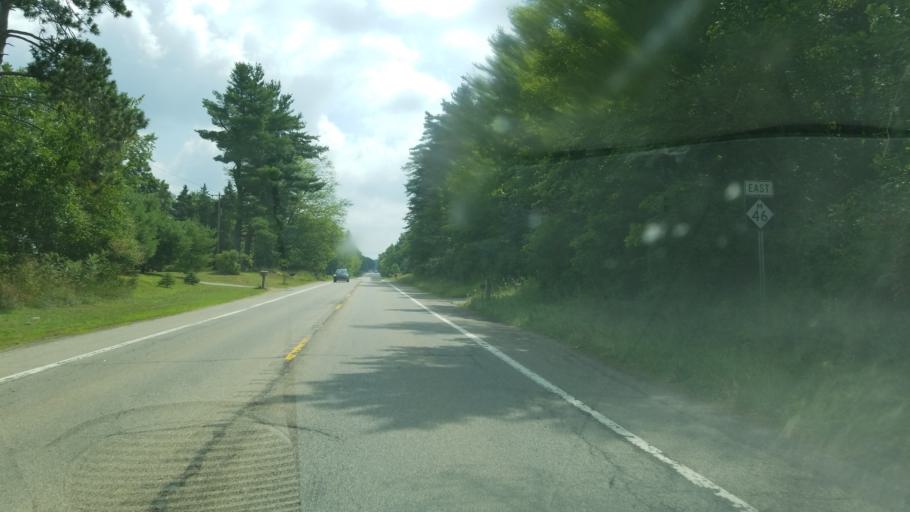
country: US
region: Michigan
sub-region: Kent County
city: Sparta
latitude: 43.2198
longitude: -85.6862
